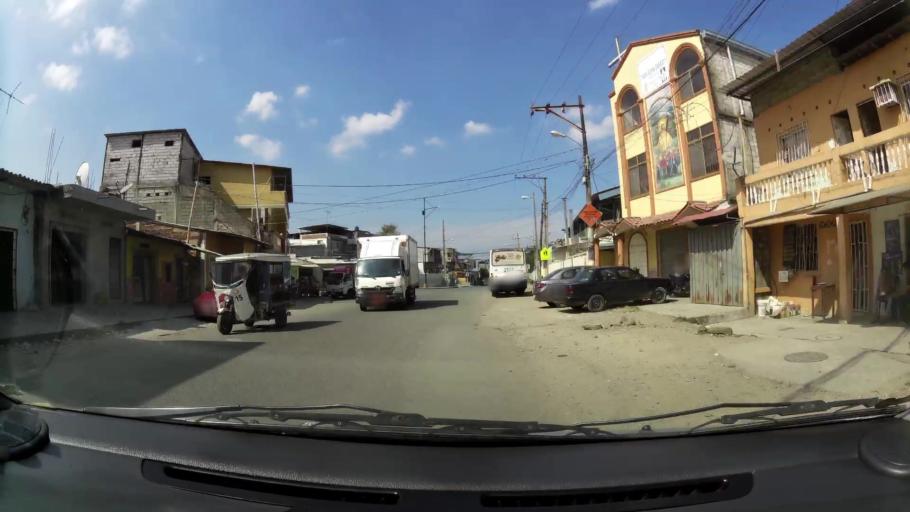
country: EC
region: Guayas
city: Guayaquil
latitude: -2.1437
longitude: -79.9412
